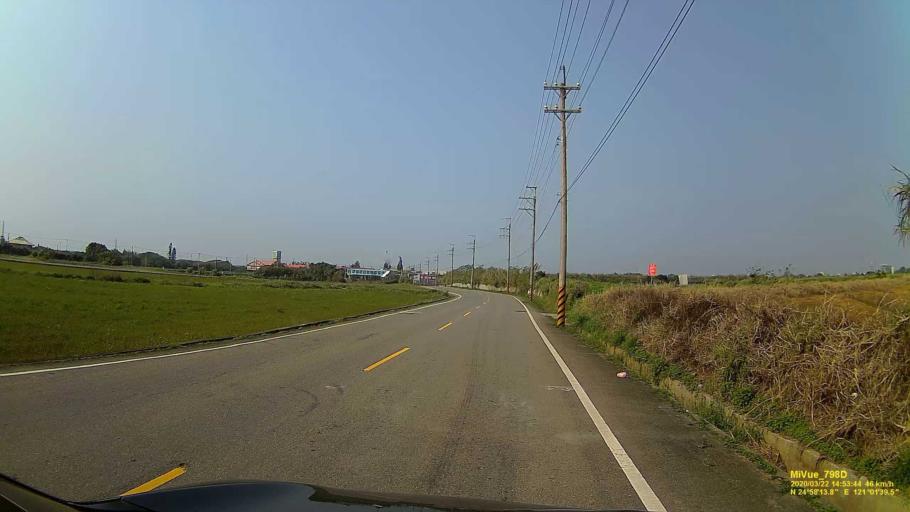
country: TW
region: Taiwan
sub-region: Hsinchu
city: Zhubei
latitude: 24.9708
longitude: 121.0277
